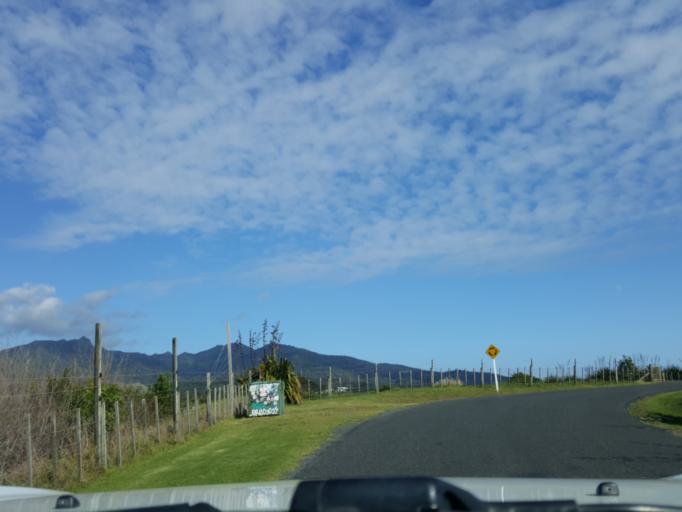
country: NZ
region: Waikato
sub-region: Waikato District
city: Raglan
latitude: -37.8186
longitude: 174.8331
